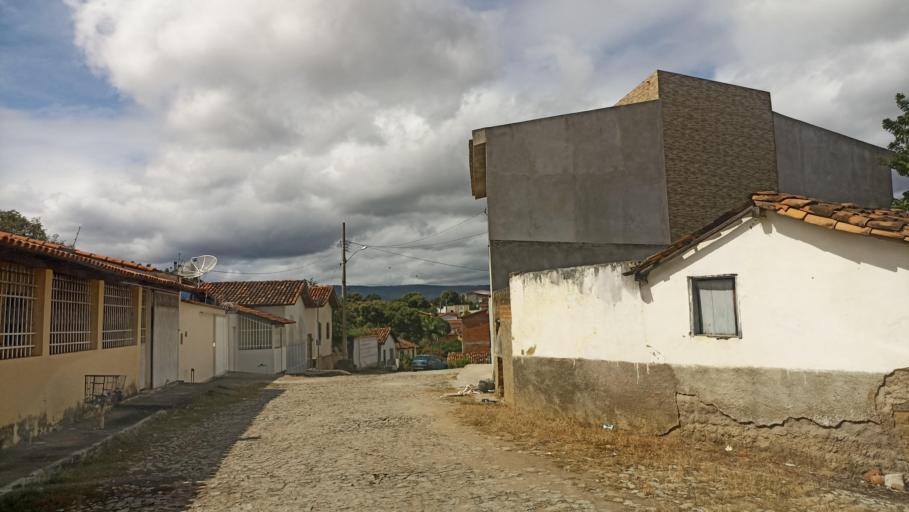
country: BR
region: Minas Gerais
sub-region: Jequitinhonha
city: Jequitinhonha
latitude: -16.4367
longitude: -41.0102
